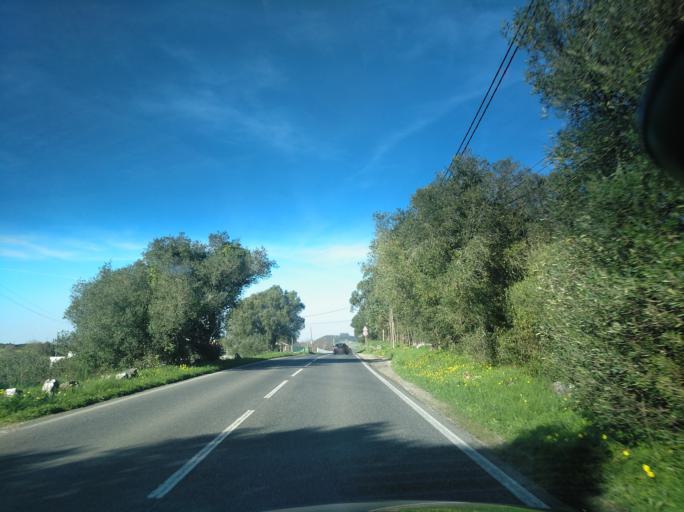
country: PT
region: Lisbon
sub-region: Sintra
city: Pero Pinheiro
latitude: 38.8758
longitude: -9.3298
